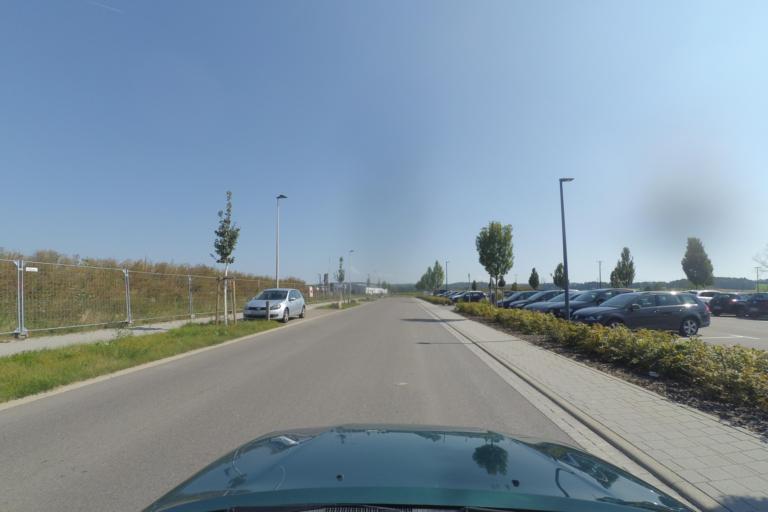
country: DE
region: Baden-Wuerttemberg
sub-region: Regierungsbezirk Stuttgart
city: Crailsheim
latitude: 49.1185
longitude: 10.0868
